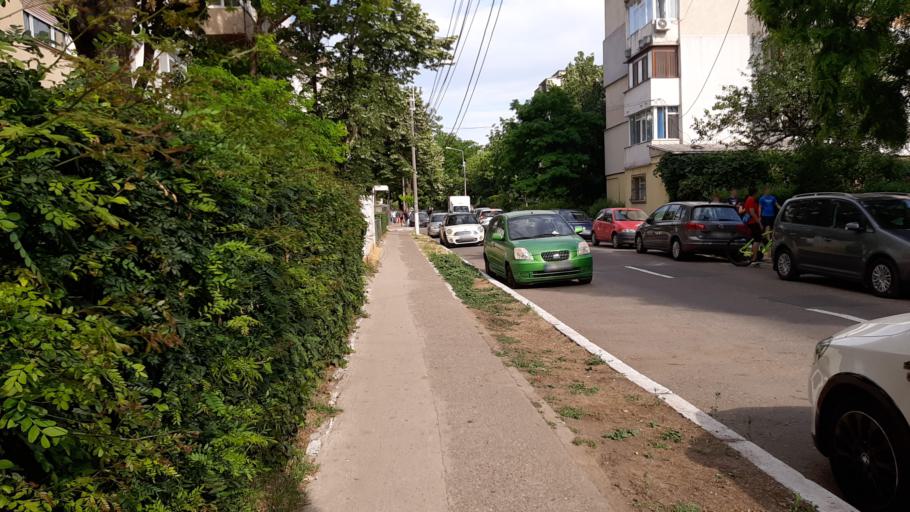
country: RO
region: Galati
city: Galati
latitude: 45.4443
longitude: 28.0236
